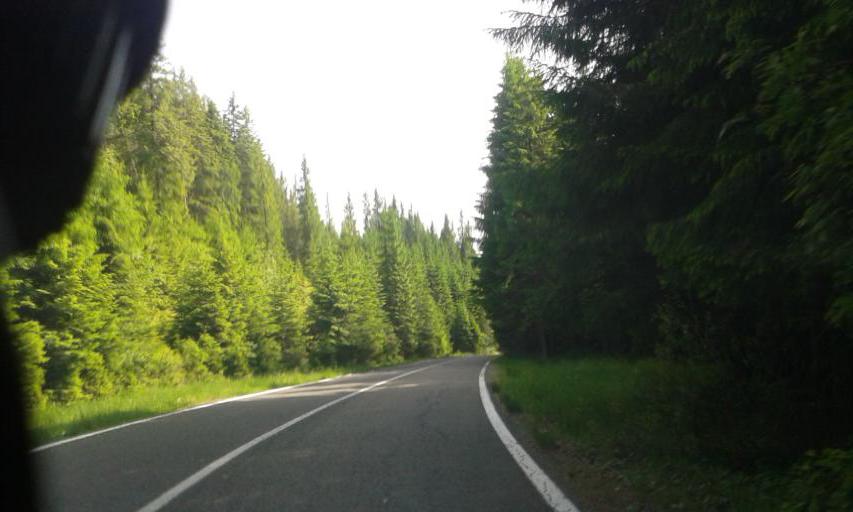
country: RO
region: Alba
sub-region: Comuna Sugag
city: Sugag
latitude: 45.5788
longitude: 23.6219
